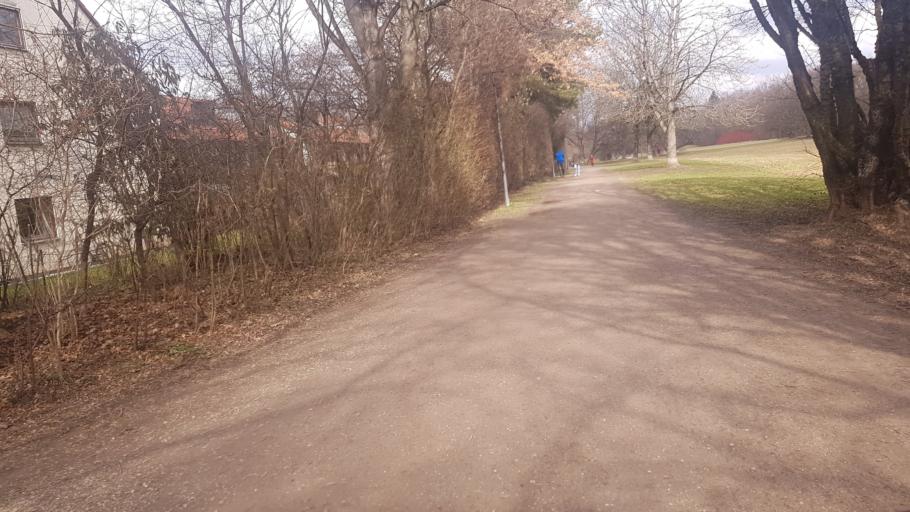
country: DE
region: Bavaria
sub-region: Upper Bavaria
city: Bogenhausen
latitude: 48.1485
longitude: 11.6333
